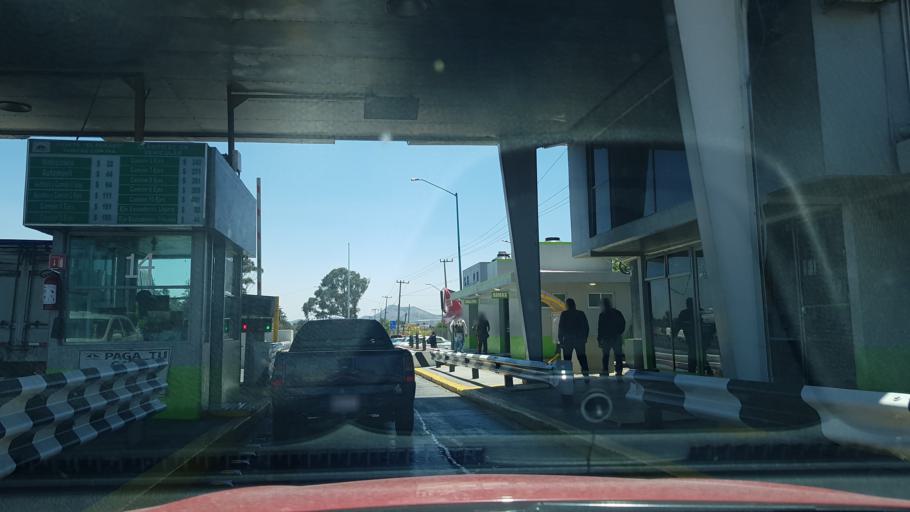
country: MX
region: Mexico
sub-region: Toluca
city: Sebastian Lerdo de Tejada
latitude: 19.4083
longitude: -99.7164
